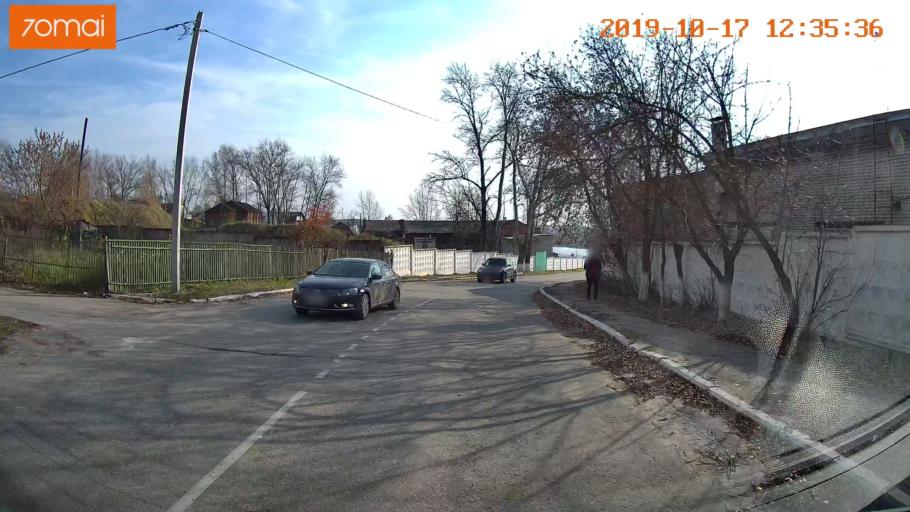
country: RU
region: Rjazan
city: Kasimov
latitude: 54.9427
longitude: 41.3703
